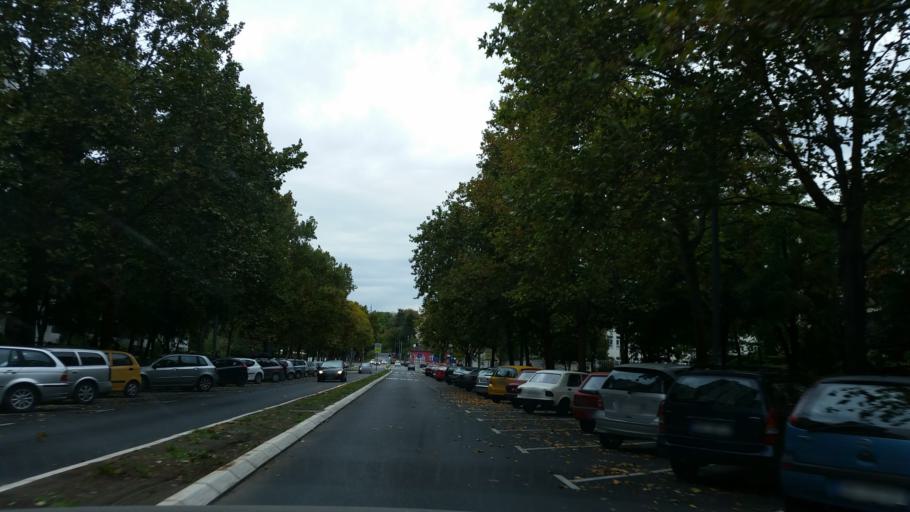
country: RS
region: Central Serbia
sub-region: Belgrade
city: Zemun
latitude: 44.8061
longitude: 20.3779
